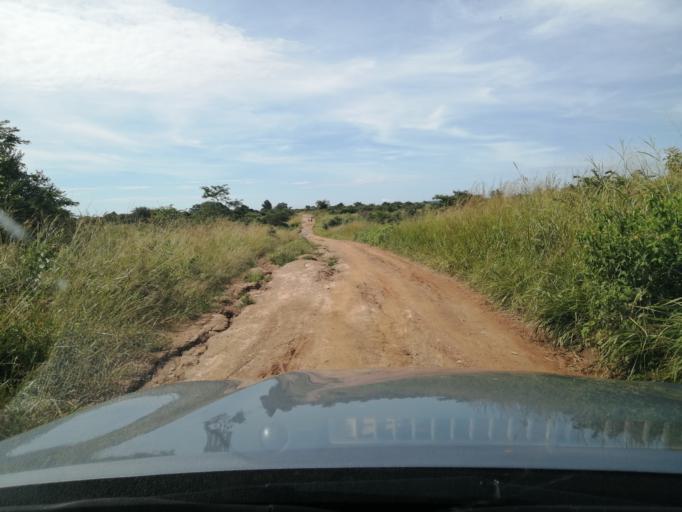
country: ZM
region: Central
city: Chibombo
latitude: -14.9474
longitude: 27.8009
